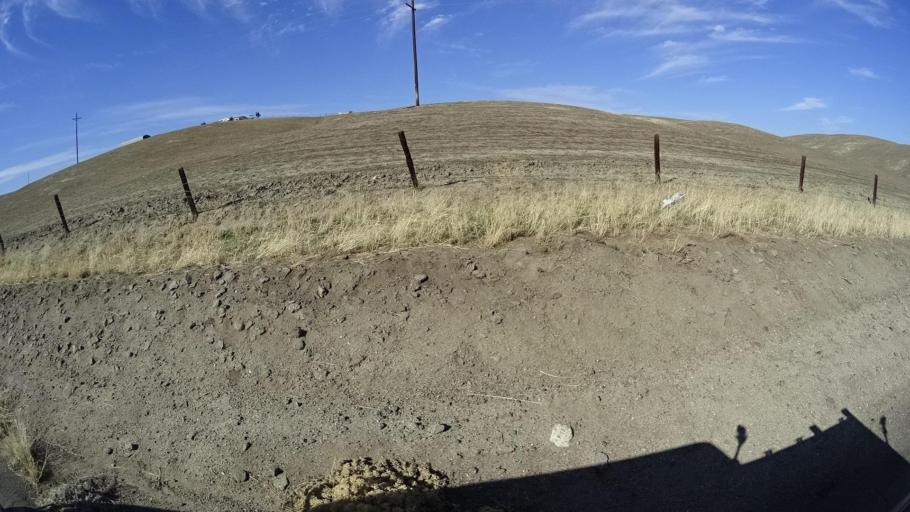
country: US
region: California
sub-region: Tulare County
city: Richgrove
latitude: 35.6365
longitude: -118.9493
